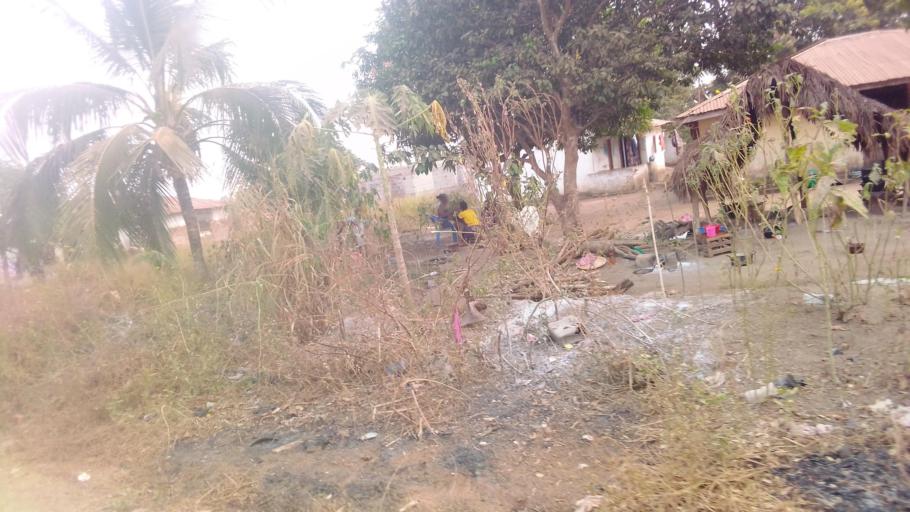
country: SL
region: Southern Province
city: Mogbwemo
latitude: 7.7776
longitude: -12.2953
